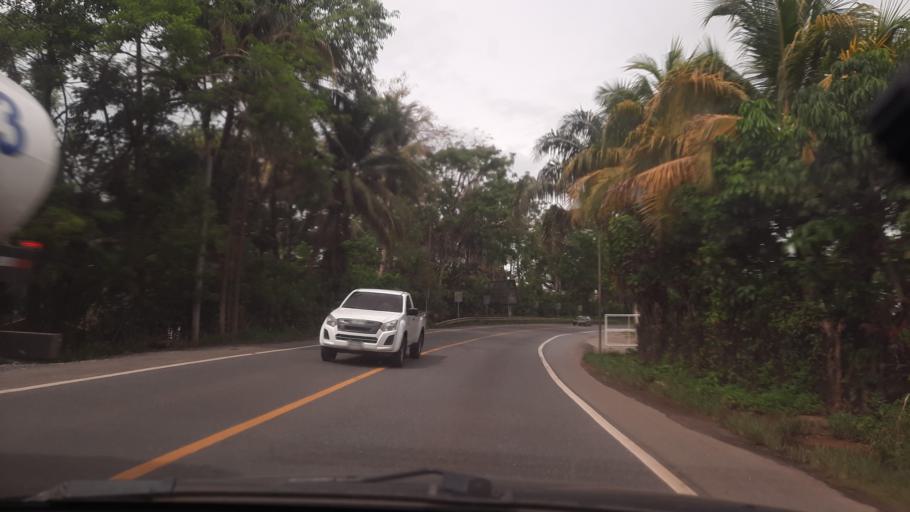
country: GT
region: Izabal
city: Morales
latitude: 15.5156
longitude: -88.7991
